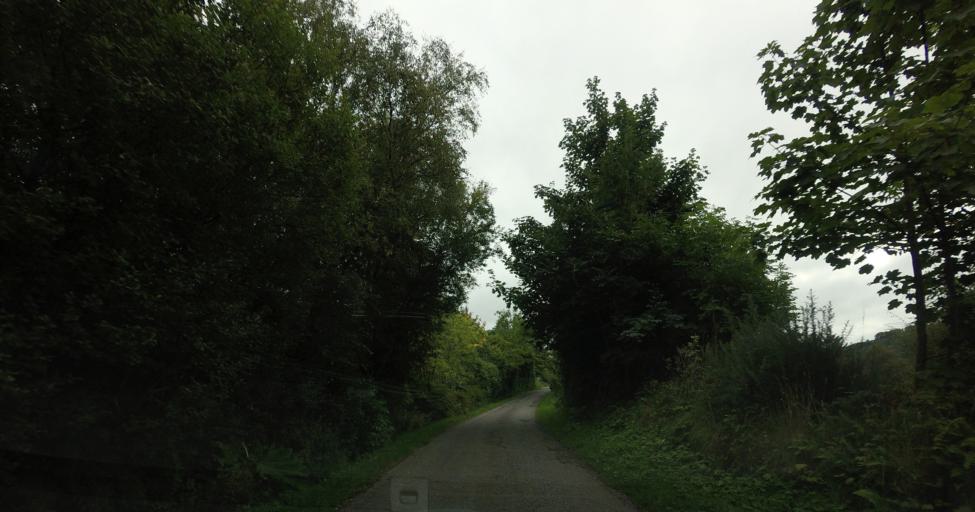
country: GB
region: Scotland
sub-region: Highland
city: Fort William
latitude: 57.2789
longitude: -5.5124
